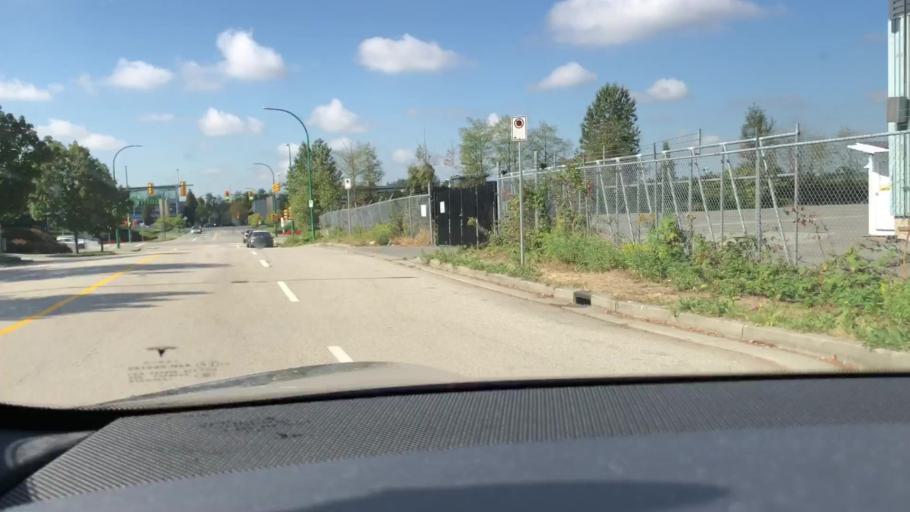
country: CA
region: British Columbia
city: New Westminster
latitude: 49.2004
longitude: -122.9778
